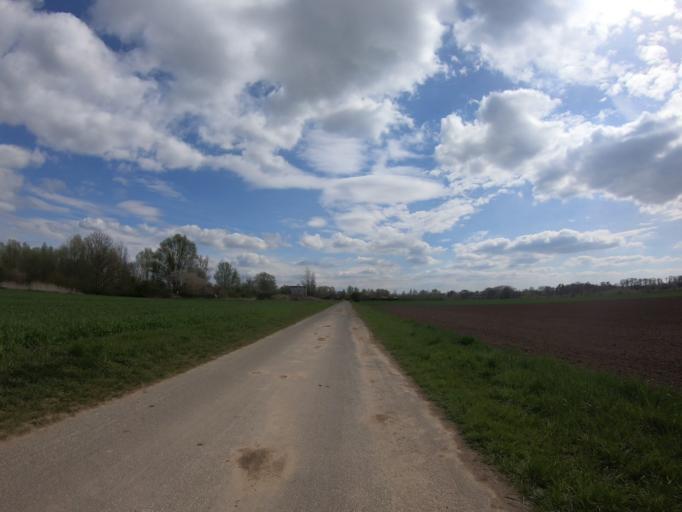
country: DE
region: Lower Saxony
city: Sarstedt
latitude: 52.2538
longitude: 9.8270
